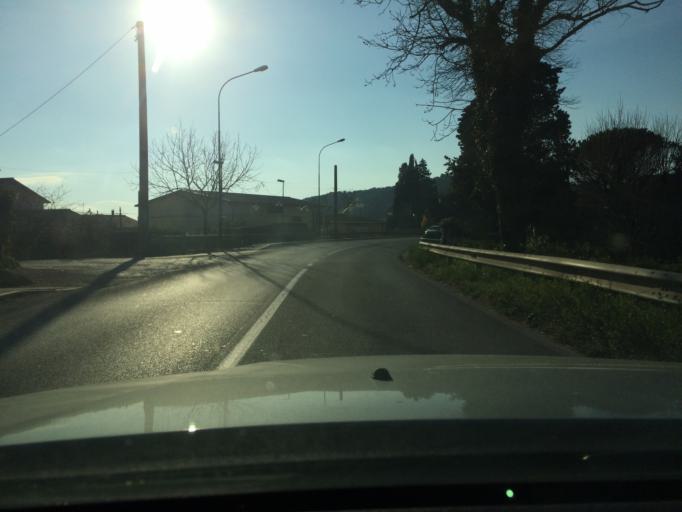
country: IT
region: Umbria
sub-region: Provincia di Terni
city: Amelia
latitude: 42.5560
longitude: 12.4316
